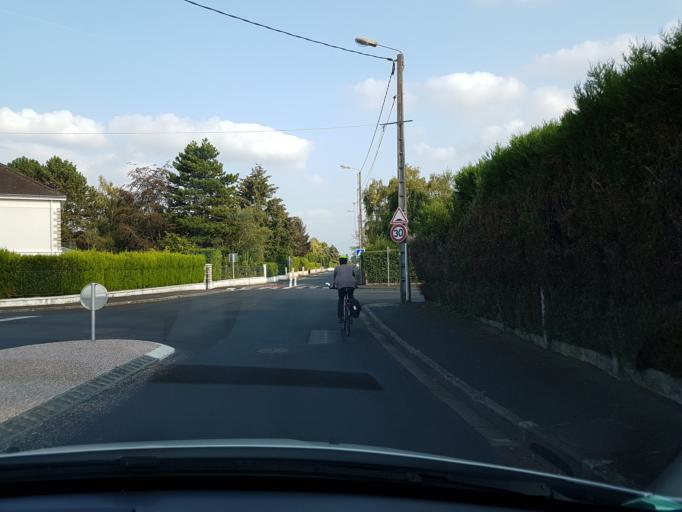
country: FR
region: Centre
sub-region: Departement d'Indre-et-Loire
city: Saint-Avertin
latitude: 47.3644
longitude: 0.7493
